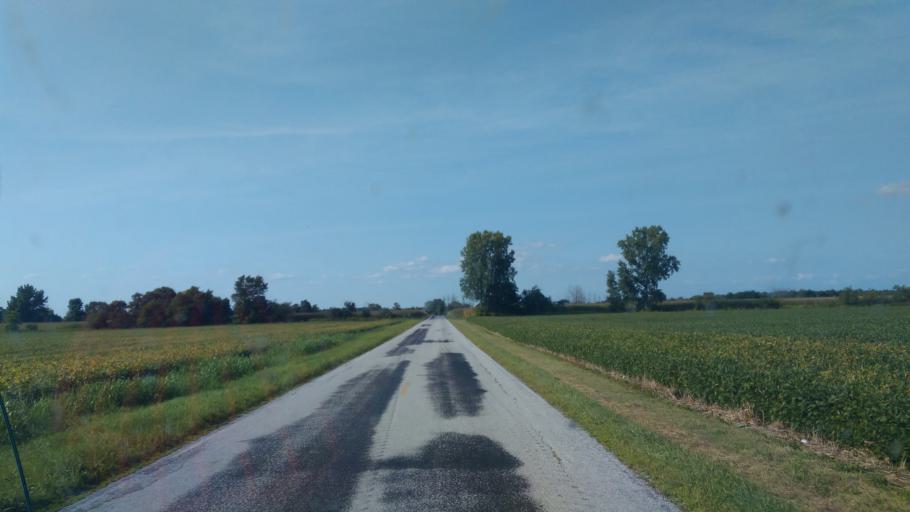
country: US
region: Ohio
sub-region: Hardin County
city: Kenton
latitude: 40.7292
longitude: -83.5737
